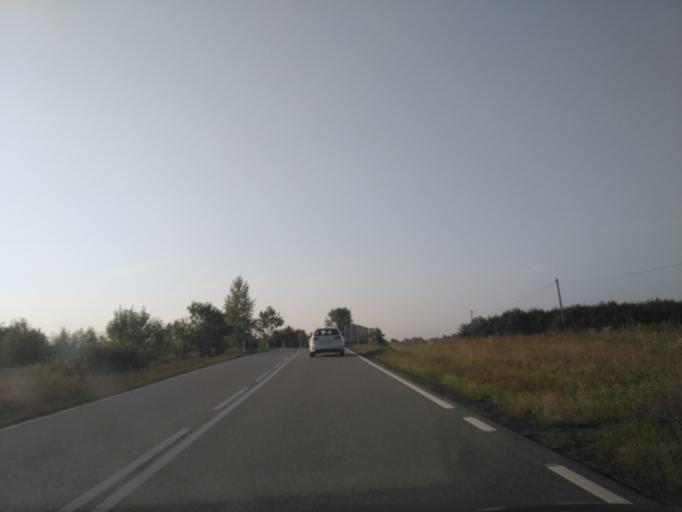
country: PL
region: Lublin Voivodeship
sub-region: Powiat janowski
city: Modliborzyce
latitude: 50.7837
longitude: 22.3225
